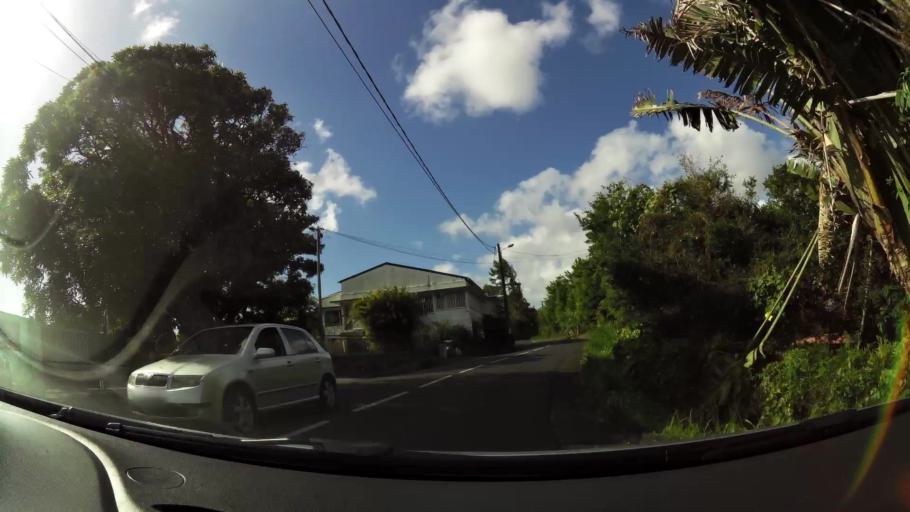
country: MQ
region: Martinique
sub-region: Martinique
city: Fort-de-France
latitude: 14.6403
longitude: -61.0745
